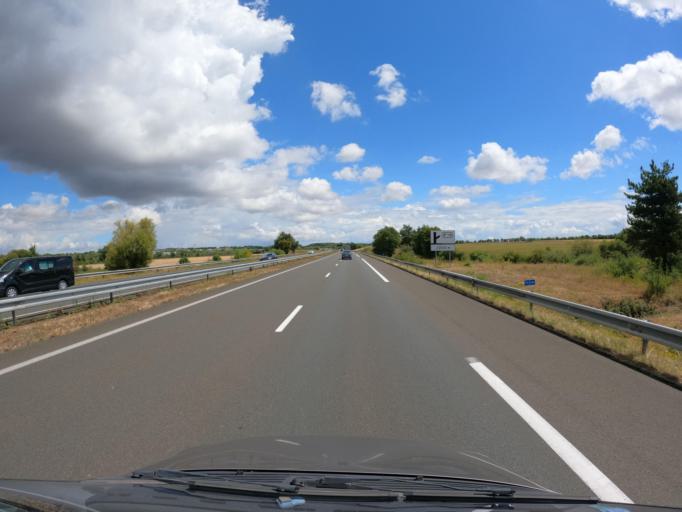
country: FR
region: Pays de la Loire
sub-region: Departement de Maine-et-Loire
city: Saint-Leger-des-Bois
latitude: 47.4498
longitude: -0.7161
